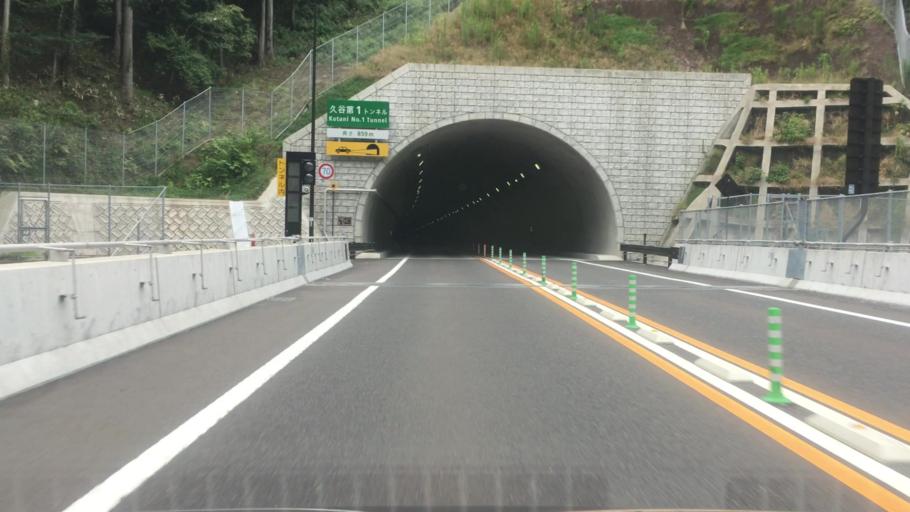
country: JP
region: Hyogo
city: Toyooka
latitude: 35.6282
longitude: 134.5233
